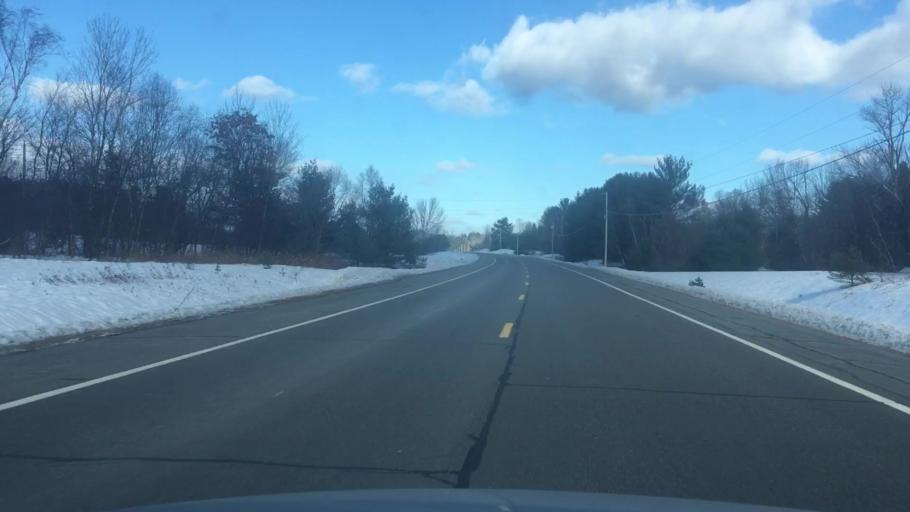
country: US
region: Maine
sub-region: Somerset County
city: Madison
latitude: 45.0146
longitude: -69.8579
